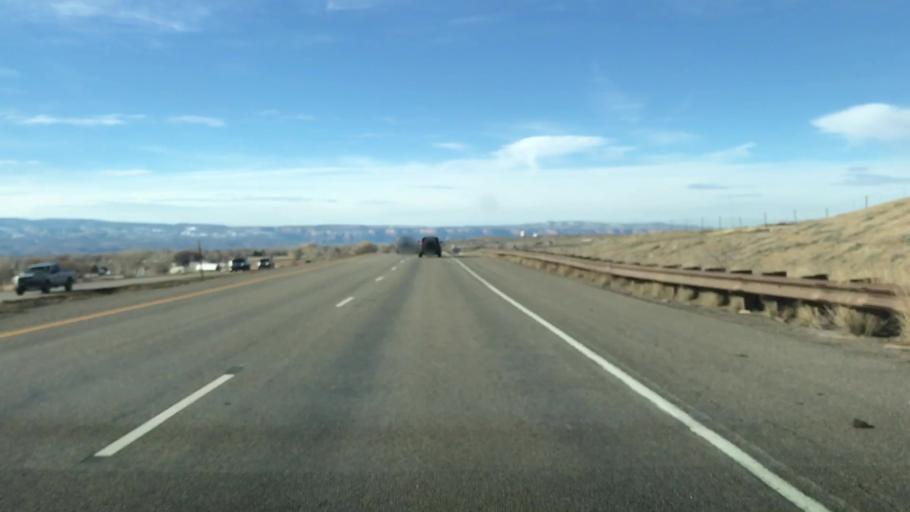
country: US
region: Colorado
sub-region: Mesa County
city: Clifton
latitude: 39.1143
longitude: -108.4100
